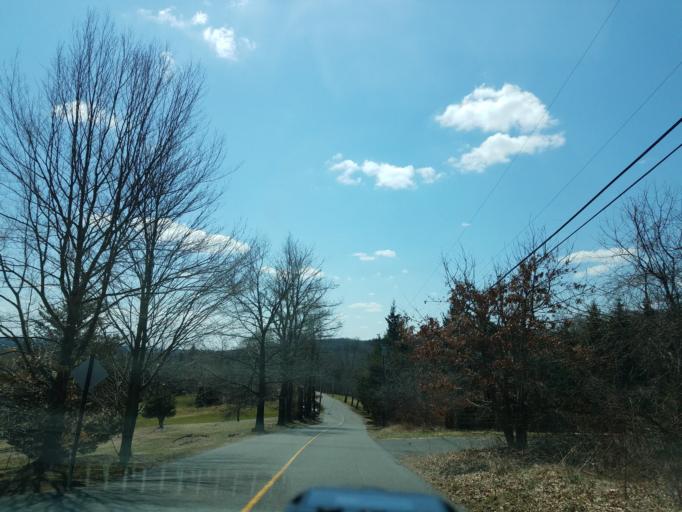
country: US
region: Connecticut
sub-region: Litchfield County
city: Bethlehem Village
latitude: 41.6163
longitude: -73.1713
